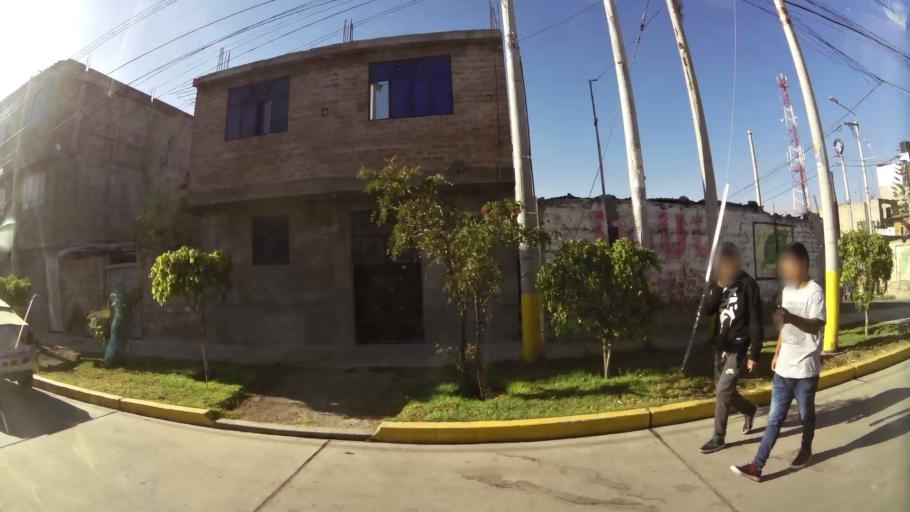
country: PE
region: Ayacucho
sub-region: Provincia de Huamanga
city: Ayacucho
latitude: -13.1512
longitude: -74.2133
